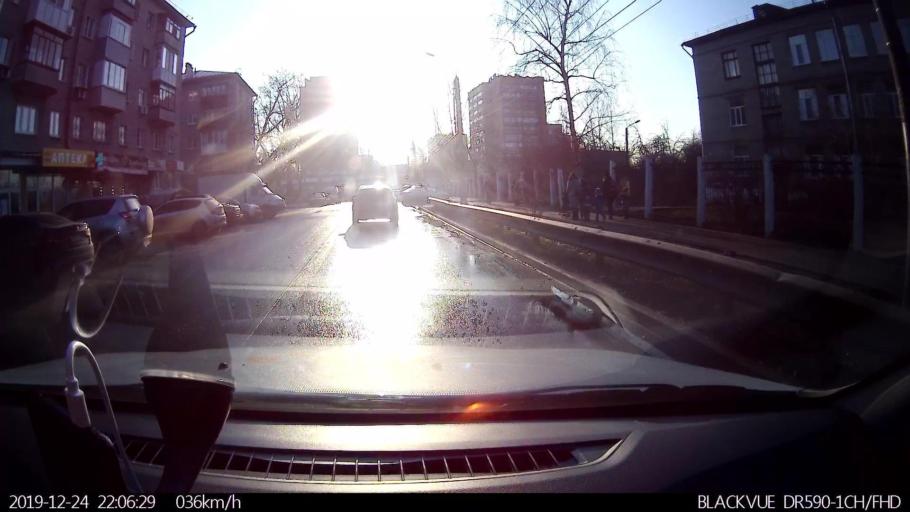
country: RU
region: Nizjnij Novgorod
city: Nizhniy Novgorod
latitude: 56.3151
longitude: 43.8828
